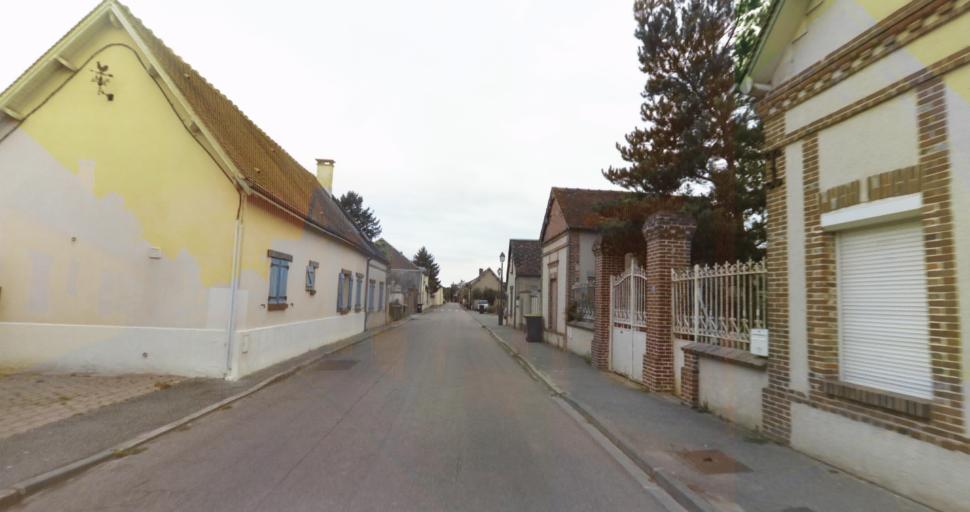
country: FR
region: Centre
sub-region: Departement d'Eure-et-Loir
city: Sorel-Moussel
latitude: 48.8651
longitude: 1.3437
